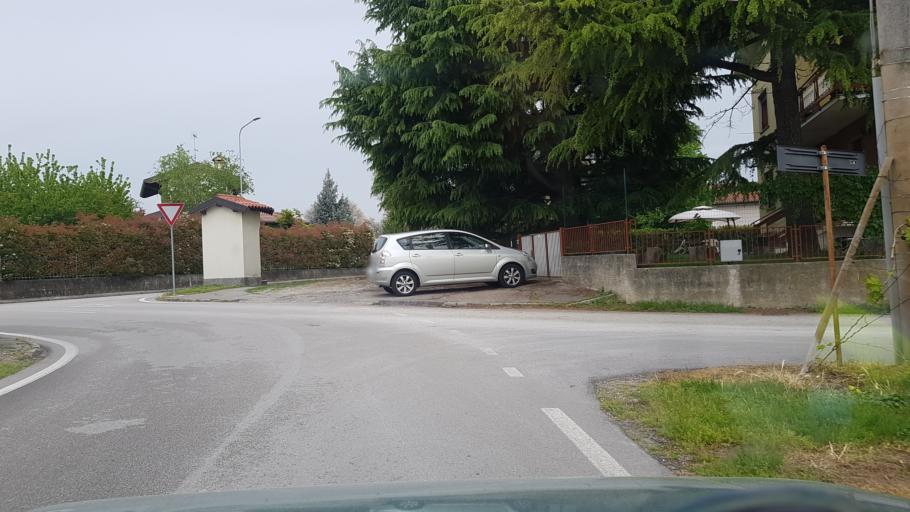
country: IT
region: Friuli Venezia Giulia
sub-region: Provincia di Gorizia
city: Ronchi dei Legionari
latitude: 45.8329
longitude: 13.5125
